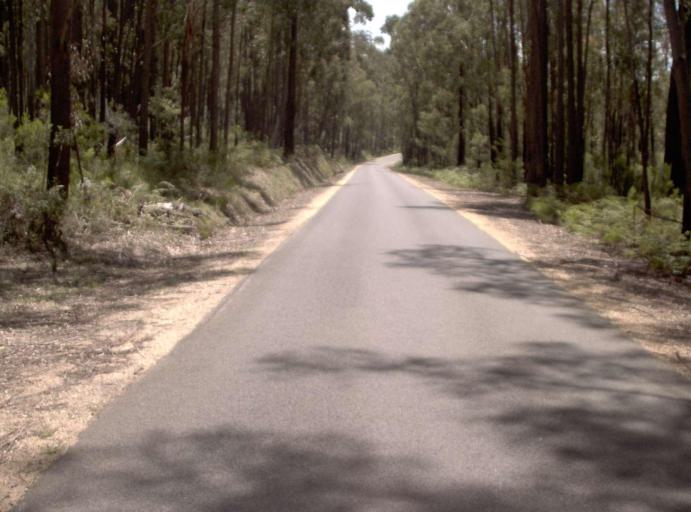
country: AU
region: New South Wales
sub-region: Bombala
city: Bombala
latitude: -37.5621
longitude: 148.9454
